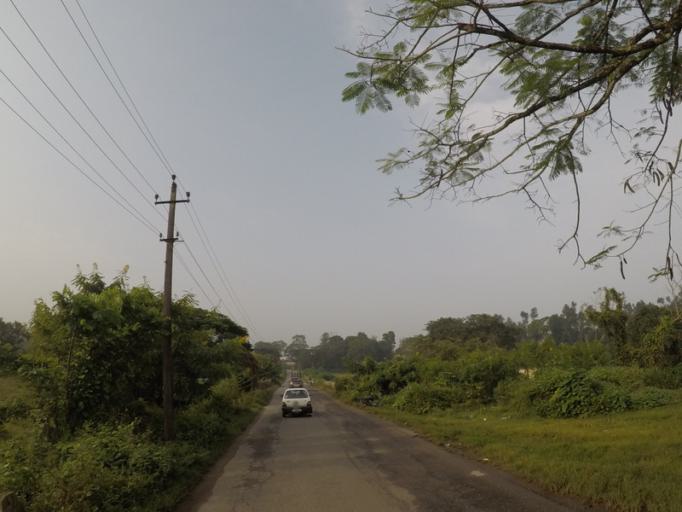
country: IN
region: Karnataka
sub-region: Chikmagalur
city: Mudigere
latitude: 13.2483
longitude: 75.6591
